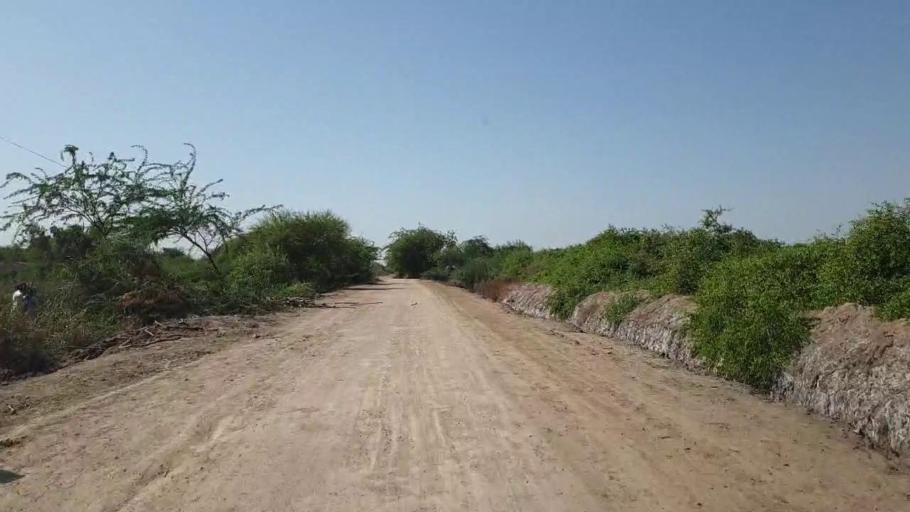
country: PK
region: Sindh
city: Tando Bago
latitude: 24.7048
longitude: 69.0383
